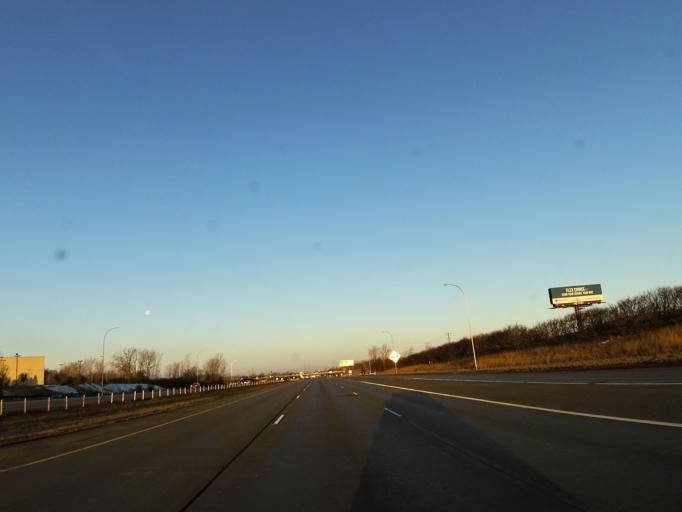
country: US
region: Minnesota
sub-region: Washington County
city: Oakdale
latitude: 44.9487
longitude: -92.9511
